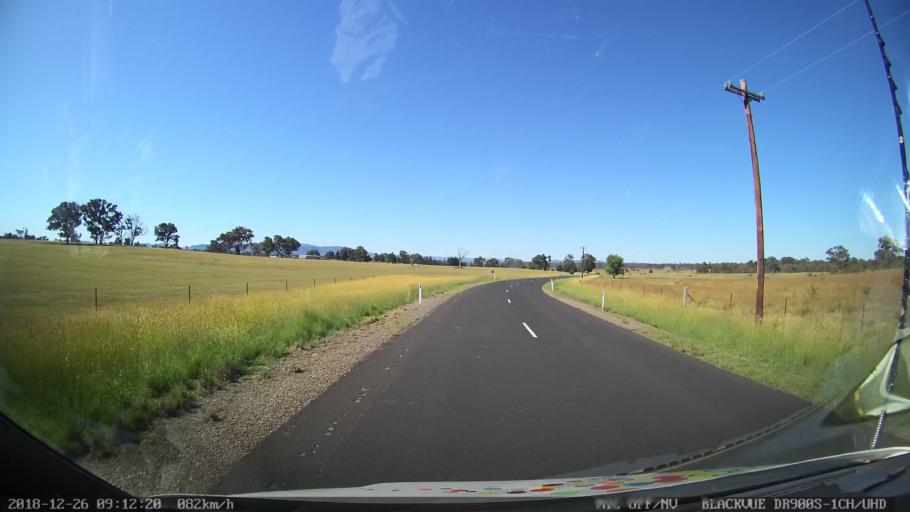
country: AU
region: New South Wales
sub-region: Mid-Western Regional
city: Kandos
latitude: -32.7567
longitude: 149.9832
